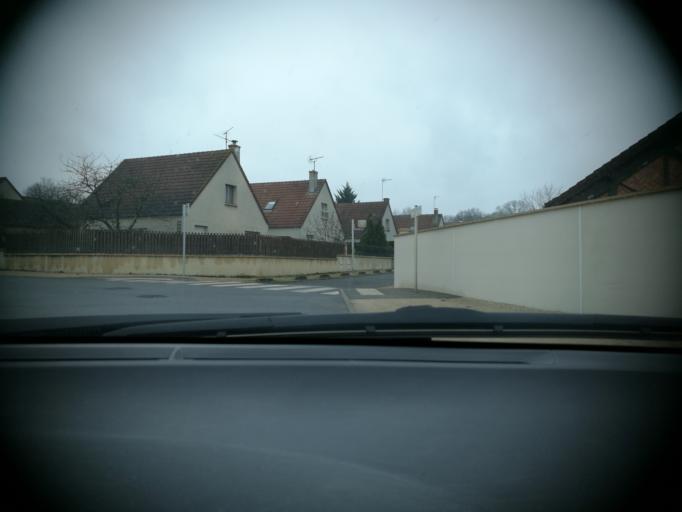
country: FR
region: Centre
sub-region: Departement du Loiret
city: Fleury-les-Aubrais
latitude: 47.9313
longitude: 1.9326
